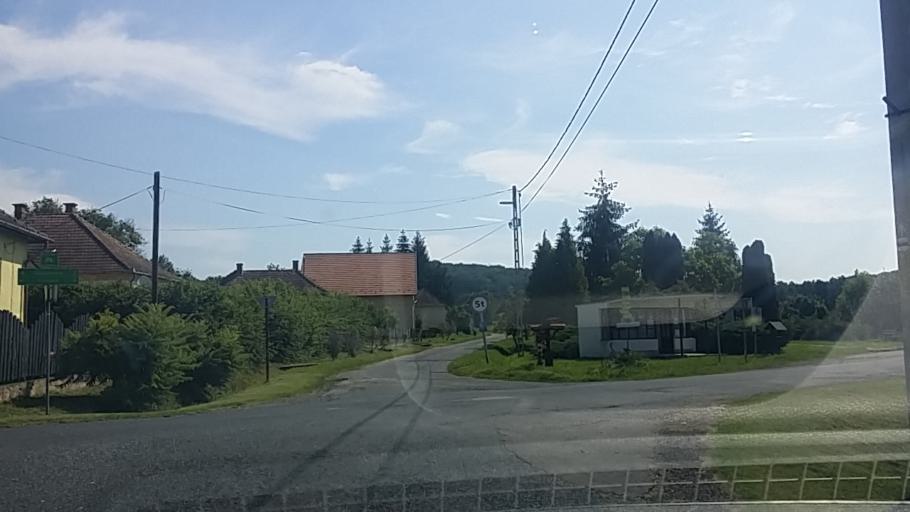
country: HU
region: Zala
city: Letenye
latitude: 46.5434
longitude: 16.6995
